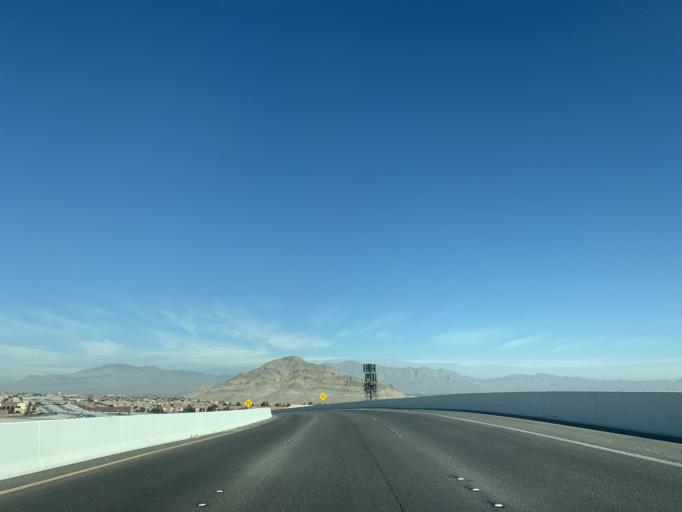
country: US
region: Nevada
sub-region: Clark County
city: Summerlin South
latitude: 36.2196
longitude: -115.3265
